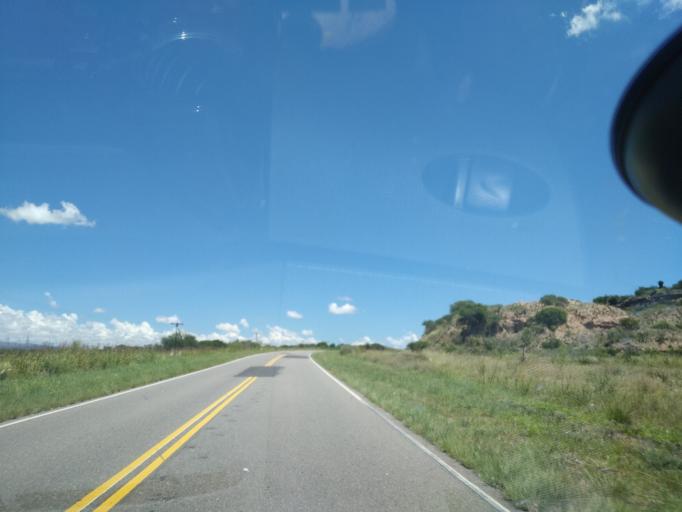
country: AR
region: Cordoba
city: Salsacate
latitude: -31.4058
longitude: -65.0962
